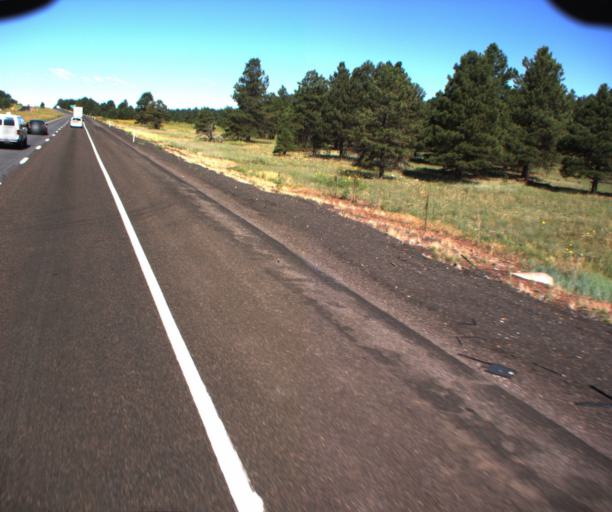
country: US
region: Arizona
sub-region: Coconino County
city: Williams
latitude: 35.2584
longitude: -112.0914
